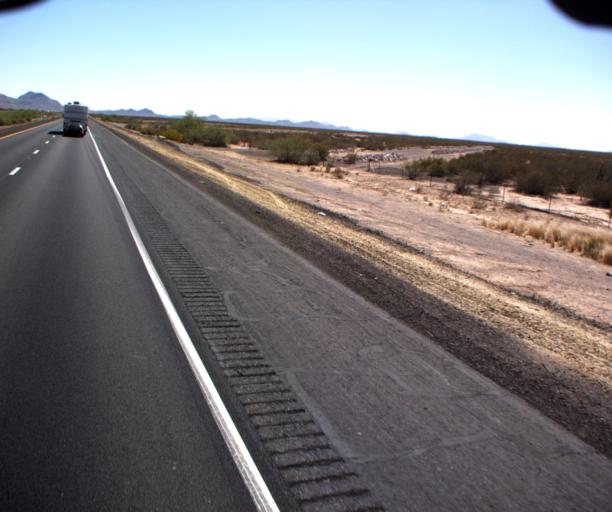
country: US
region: Arizona
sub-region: La Paz County
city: Salome
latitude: 33.6247
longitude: -113.7270
